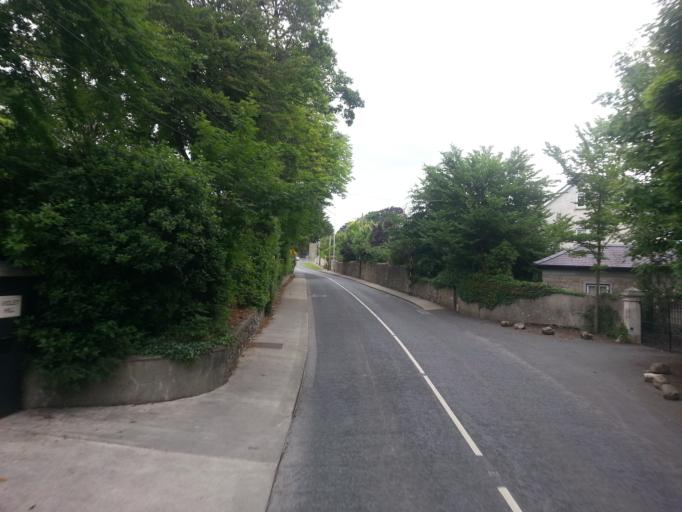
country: IE
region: Leinster
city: Sandyford
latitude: 53.2612
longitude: -6.2108
